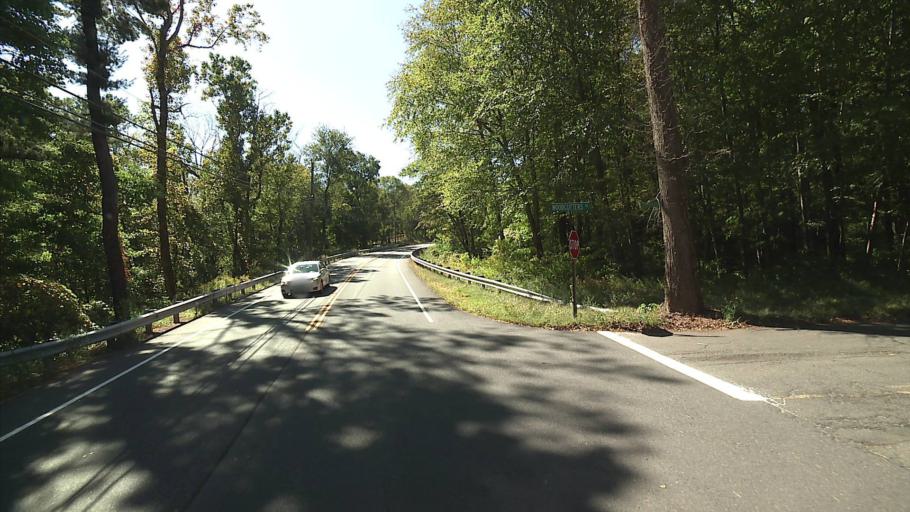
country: US
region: Connecticut
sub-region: New Haven County
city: Prospect
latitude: 41.4518
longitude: -72.9685
